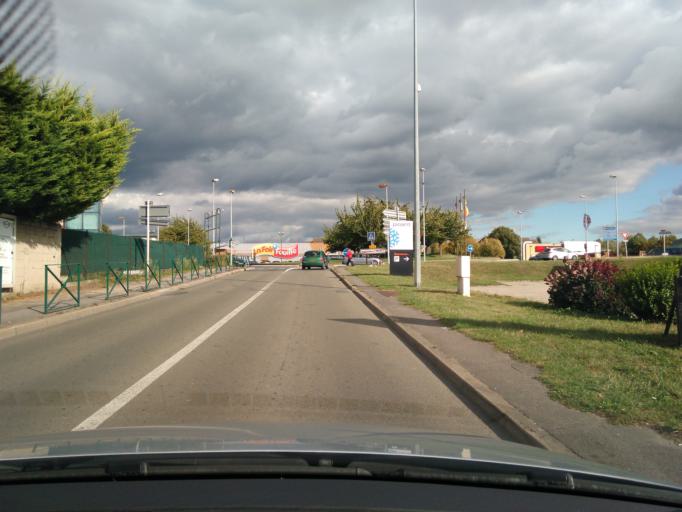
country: FR
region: Ile-de-France
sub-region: Departement de Seine-et-Marne
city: Meaux
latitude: 48.9422
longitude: 2.8783
